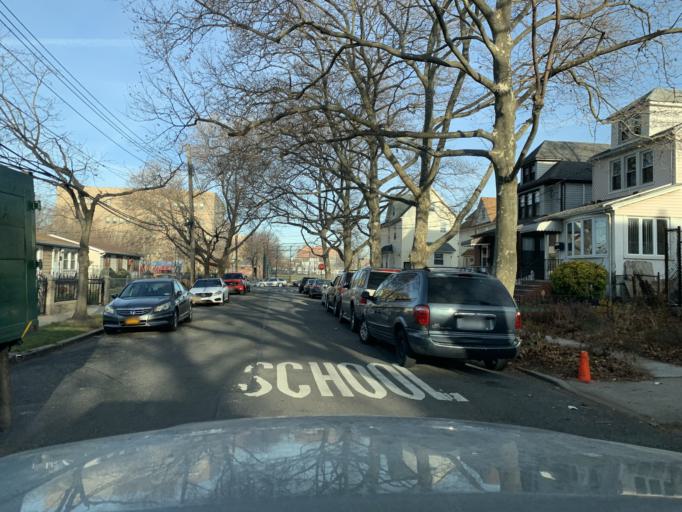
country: US
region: New York
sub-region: Queens County
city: Jamaica
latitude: 40.6923
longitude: -73.7947
